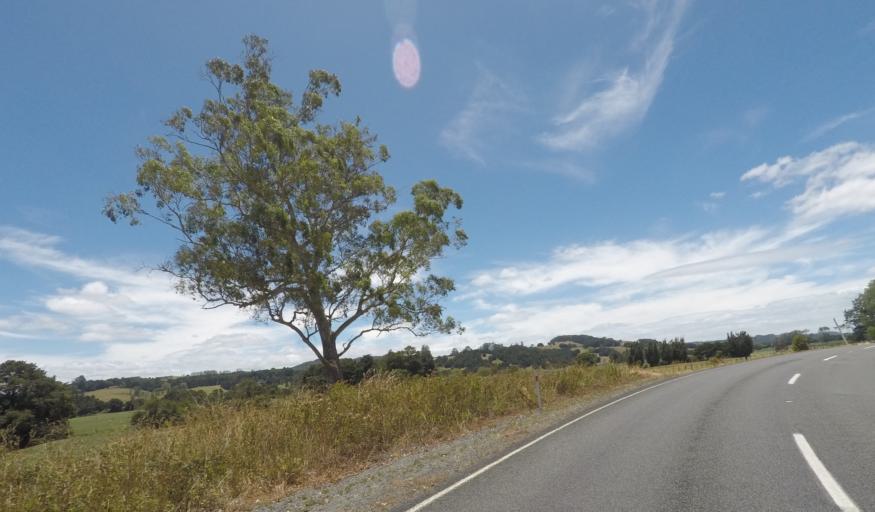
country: NZ
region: Northland
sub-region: Whangarei
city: Whangarei
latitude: -35.5372
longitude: 174.3104
